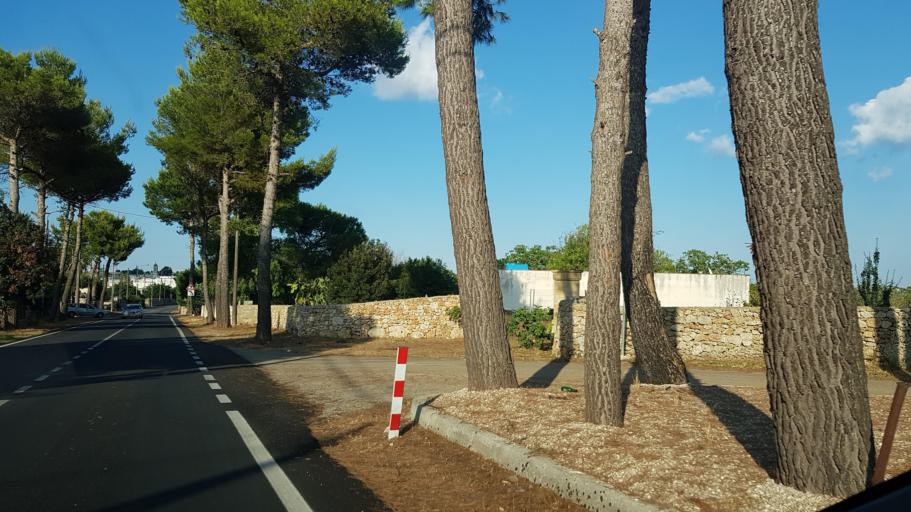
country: IT
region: Apulia
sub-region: Provincia di Lecce
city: Castiglione
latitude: 39.9788
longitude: 18.3404
